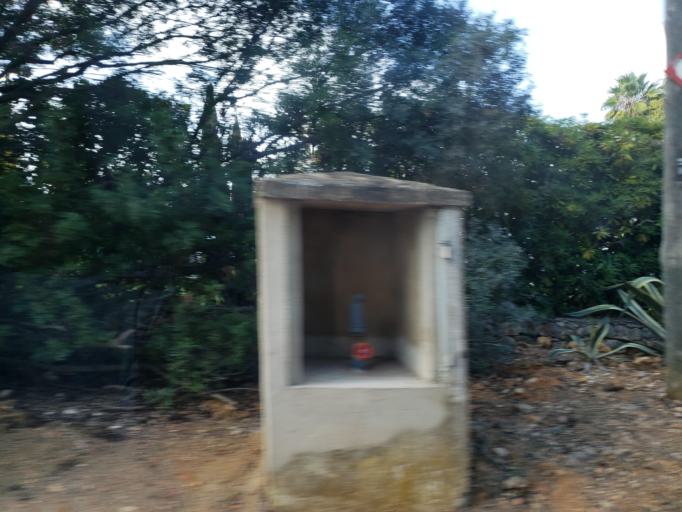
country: PT
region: Faro
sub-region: Portimao
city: Alvor
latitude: 37.1845
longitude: -8.5858
